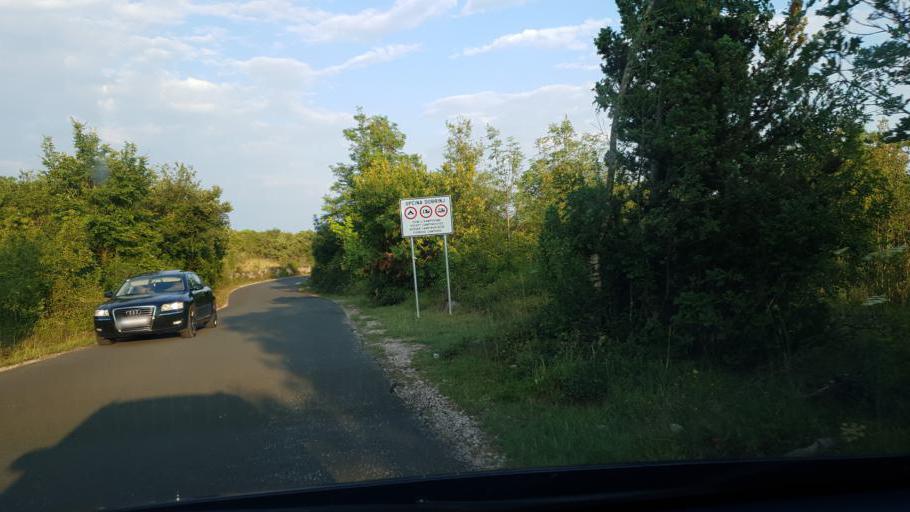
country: HR
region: Primorsko-Goranska
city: Omisalj
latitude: 45.1818
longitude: 14.5920
